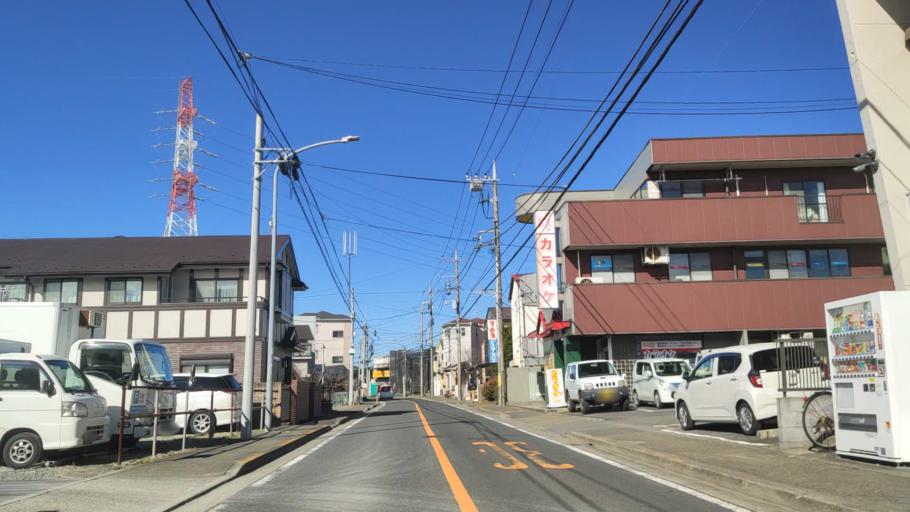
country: JP
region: Kanagawa
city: Minami-rinkan
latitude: 35.4888
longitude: 139.5186
